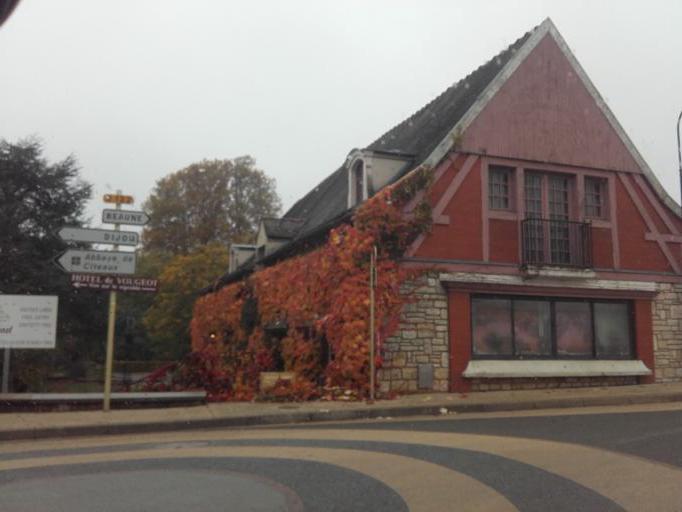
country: FR
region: Bourgogne
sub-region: Departement de la Cote-d'Or
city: Nuits-Saint-Georges
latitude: 47.1750
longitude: 4.9634
